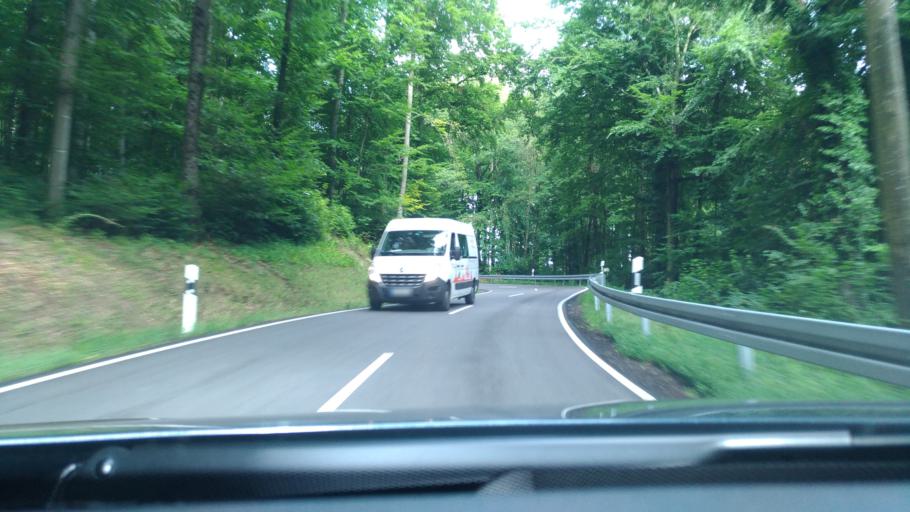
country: DE
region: Baden-Wuerttemberg
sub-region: Freiburg Region
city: Bodman-Ludwigshafen
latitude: 47.8247
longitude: 9.0646
